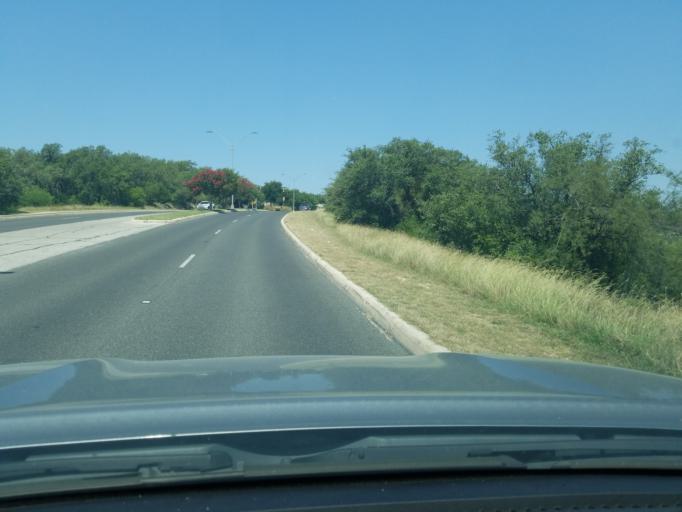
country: US
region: Texas
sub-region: Bexar County
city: Hollywood Park
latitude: 29.6392
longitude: -98.4779
